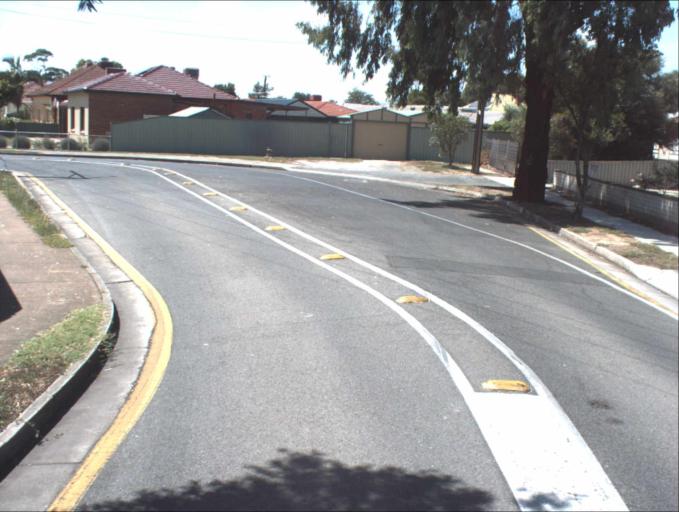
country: AU
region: South Australia
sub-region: Port Adelaide Enfield
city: Alberton
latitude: -34.8571
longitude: 138.5235
